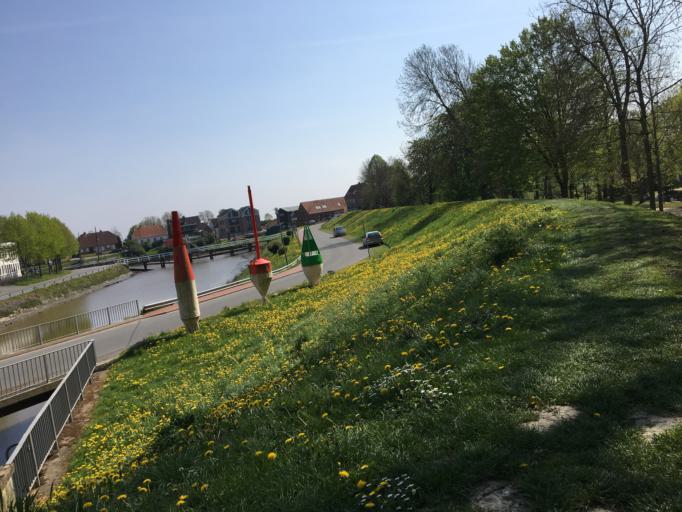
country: DE
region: Schleswig-Holstein
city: Tonning
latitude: 54.3158
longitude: 8.9428
